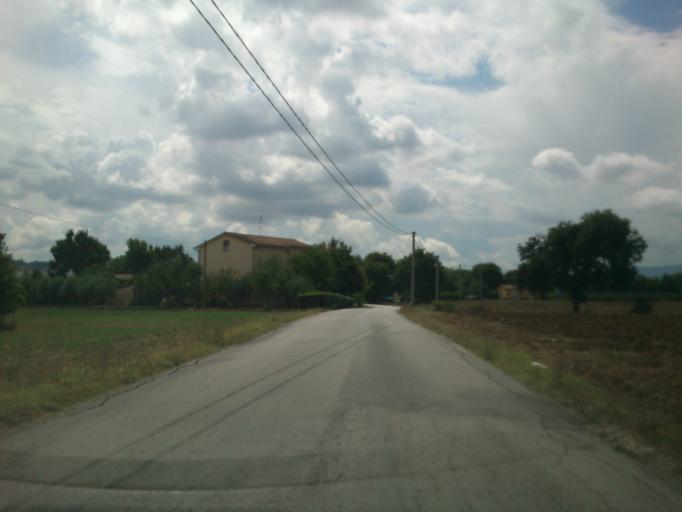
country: IT
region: The Marches
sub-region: Provincia di Pesaro e Urbino
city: Villanova
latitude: 43.7377
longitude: 12.9260
